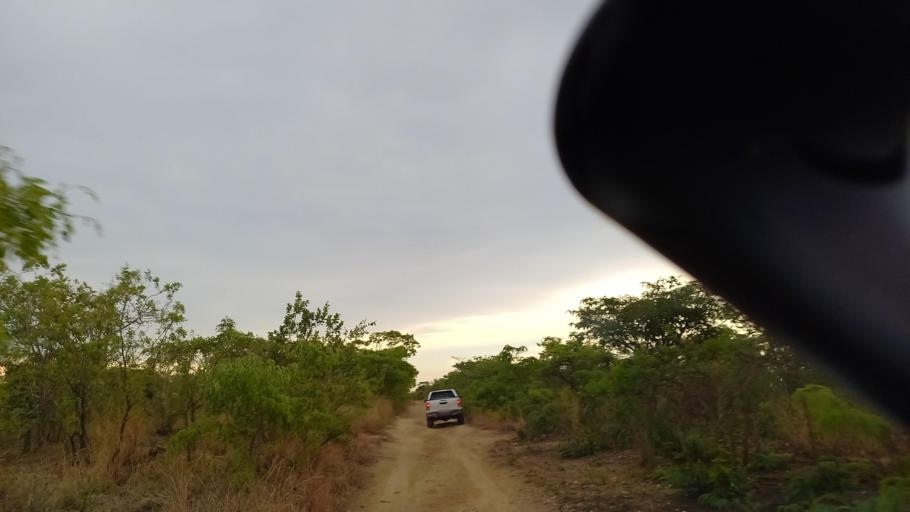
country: ZM
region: Lusaka
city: Kafue
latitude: -16.0481
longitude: 28.3282
